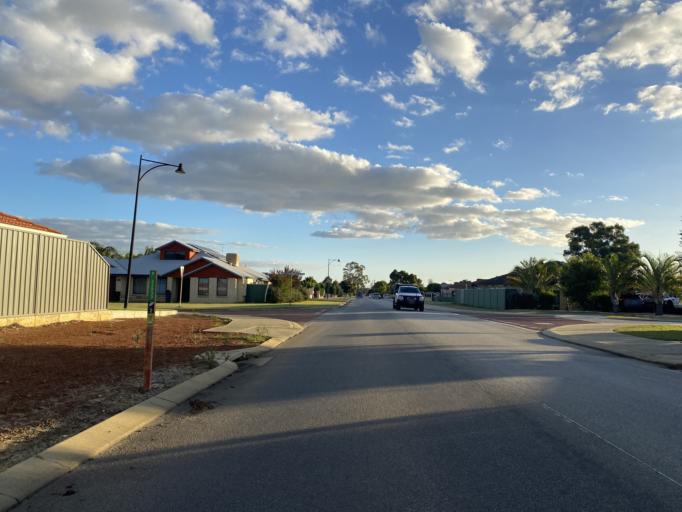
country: AU
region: Western Australia
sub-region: Kalamunda
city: Maida Vale
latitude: -31.9697
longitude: 116.0064
